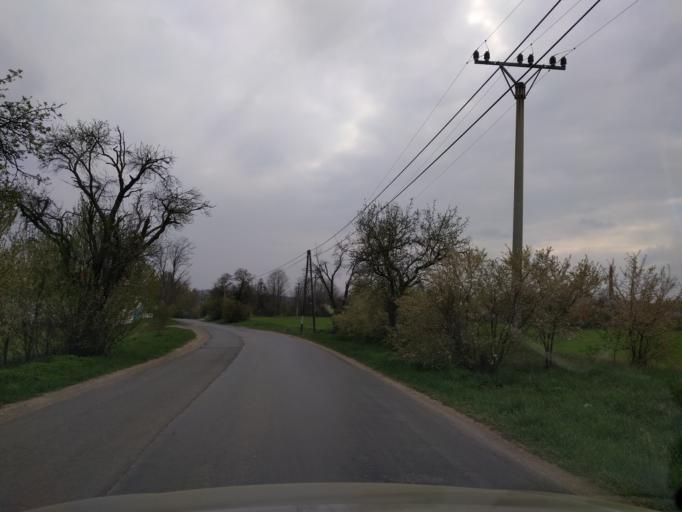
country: CZ
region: Central Bohemia
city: Cesky Brod
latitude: 50.0614
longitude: 14.8475
